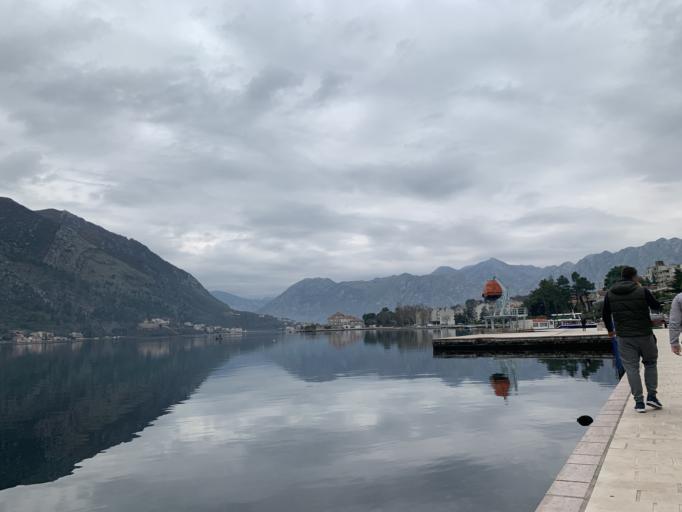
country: ME
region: Kotor
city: Kotor
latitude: 42.4323
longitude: 18.7672
